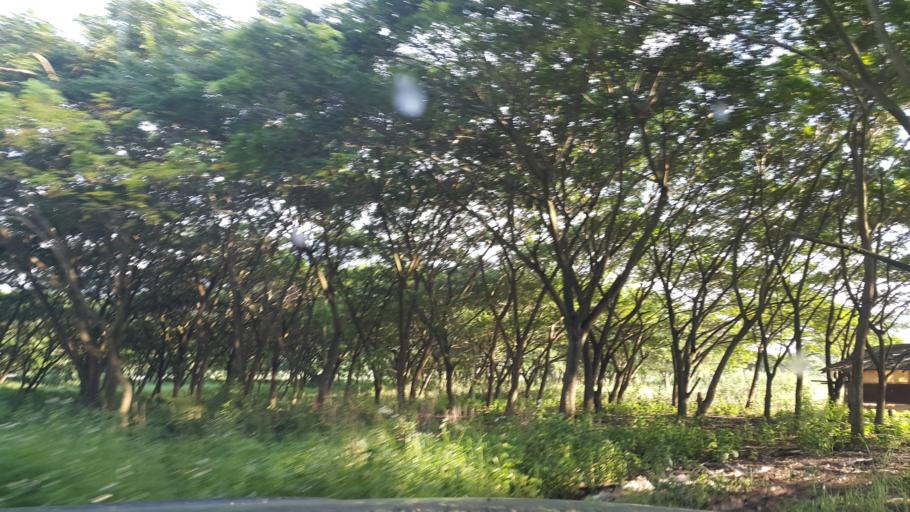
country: TH
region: Chiang Mai
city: Mae On
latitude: 18.7439
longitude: 99.2354
